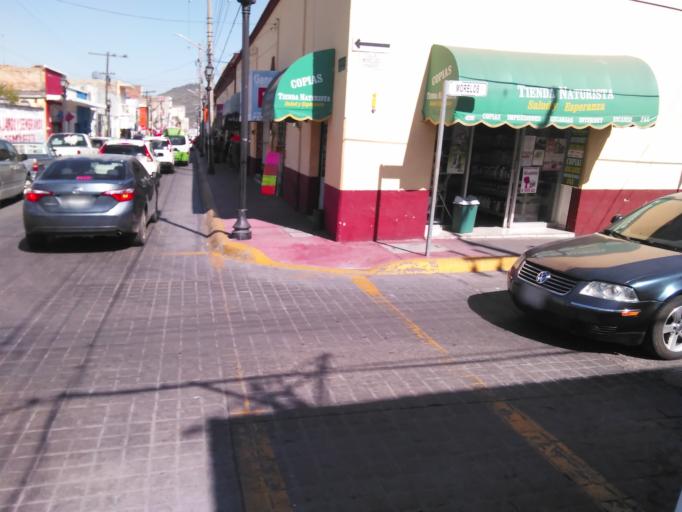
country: MX
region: Nayarit
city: Tepic
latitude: 21.5106
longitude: -104.8961
